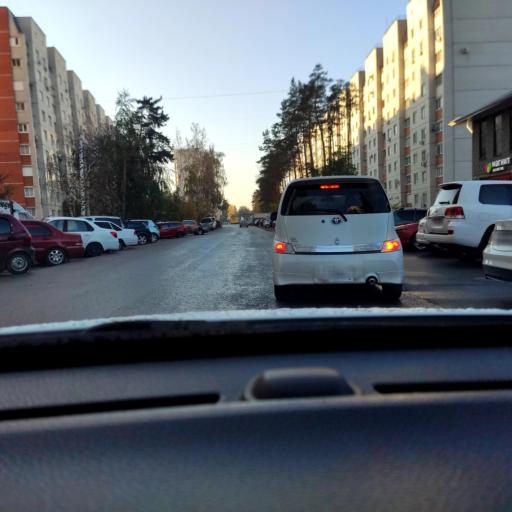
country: RU
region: Voronezj
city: Voronezh
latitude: 51.6919
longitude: 39.2797
